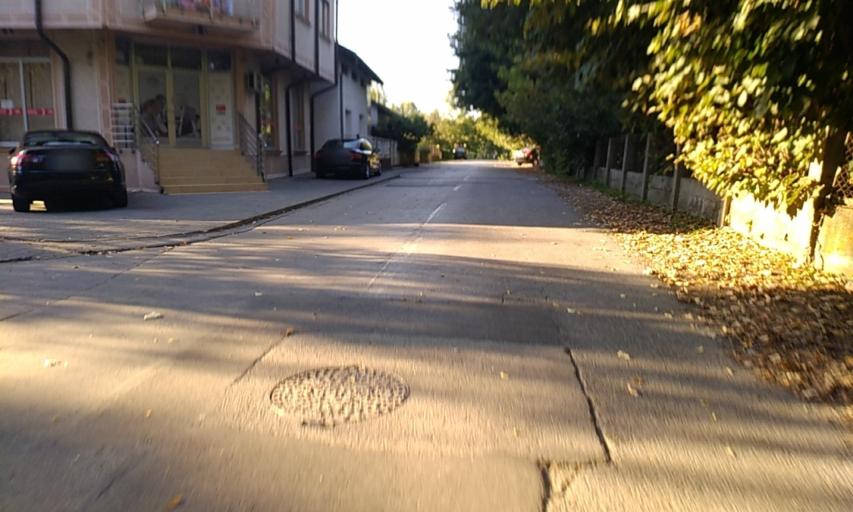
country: BA
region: Republika Srpska
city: Mejdan - Obilicevo
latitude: 44.7645
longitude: 17.1960
